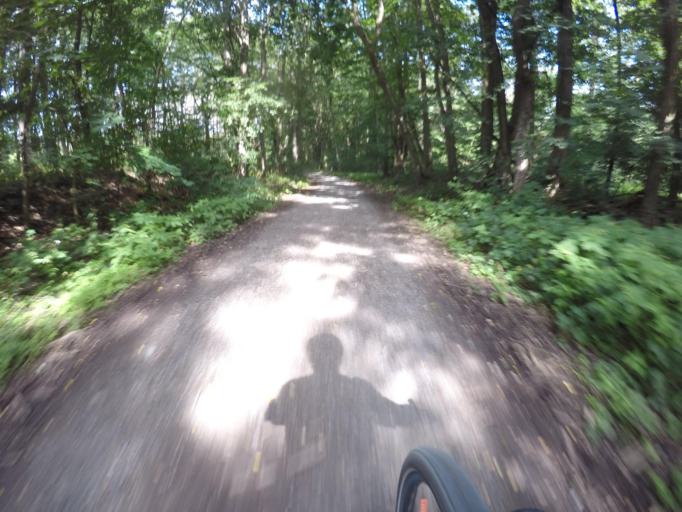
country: DE
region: Baden-Wuerttemberg
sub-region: Karlsruhe Region
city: Otisheim
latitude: 48.9801
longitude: 8.7862
